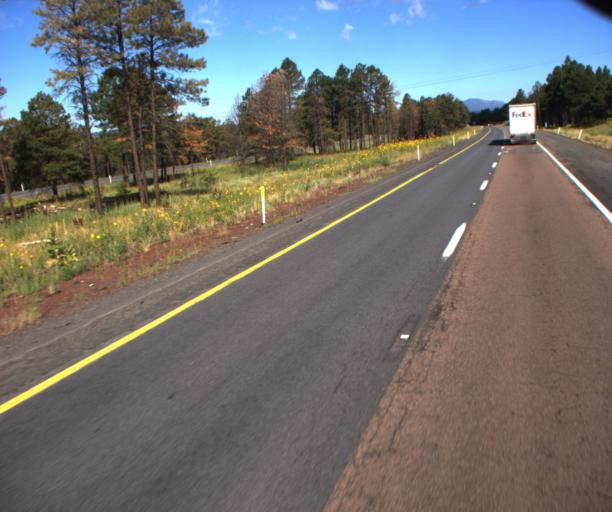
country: US
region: Arizona
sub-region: Coconino County
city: Flagstaff
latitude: 35.2219
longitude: -111.7929
